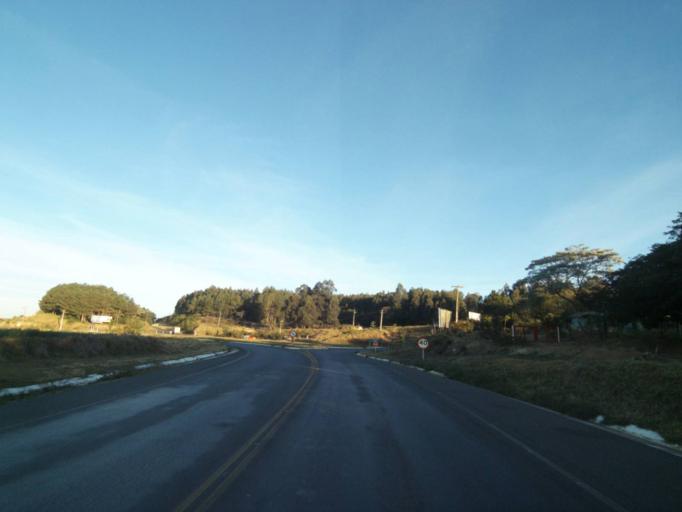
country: BR
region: Parana
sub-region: Tibagi
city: Tibagi
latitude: -24.4998
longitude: -50.4454
